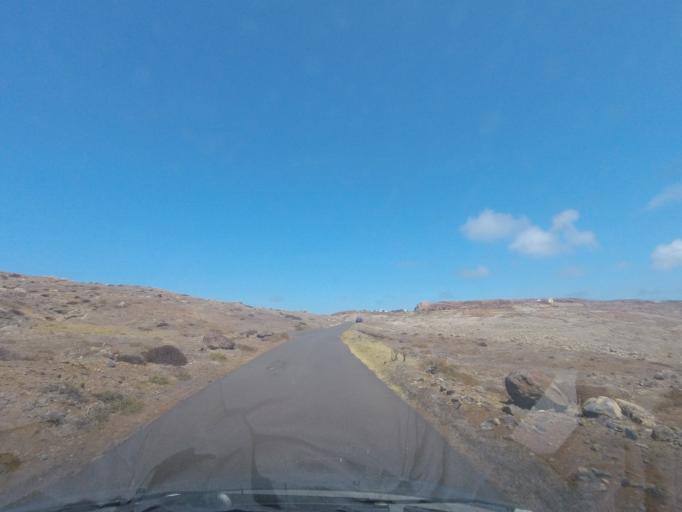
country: PT
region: Madeira
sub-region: Machico
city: Canical
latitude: 32.7492
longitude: -16.7098
